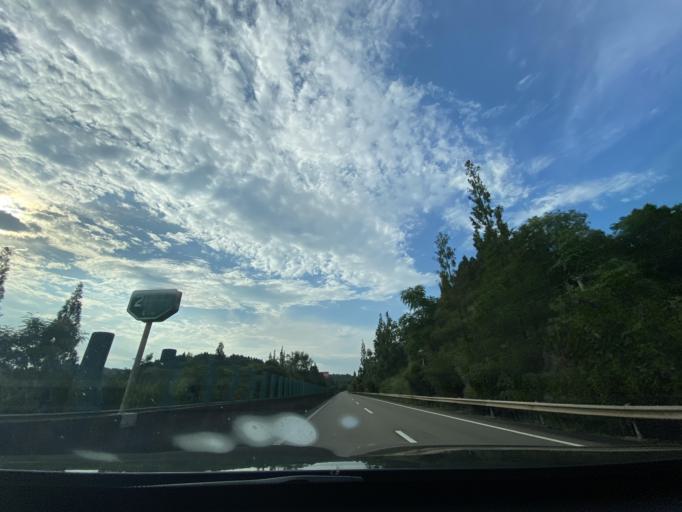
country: CN
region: Sichuan
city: Jiancheng
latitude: 30.2600
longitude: 104.6079
